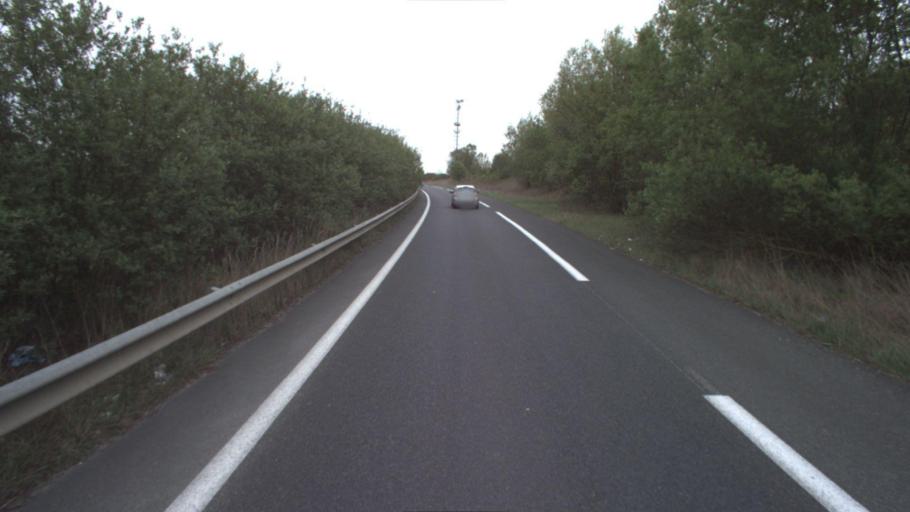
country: FR
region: Ile-de-France
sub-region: Departement de Seine-et-Marne
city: Mareuil-les-Meaux
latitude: 48.9164
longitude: 2.8697
